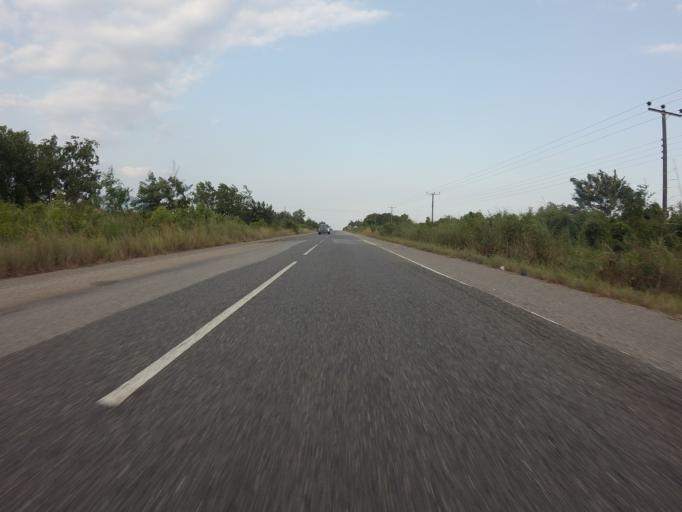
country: GH
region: Volta
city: Anloga
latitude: 6.0861
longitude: 0.5499
